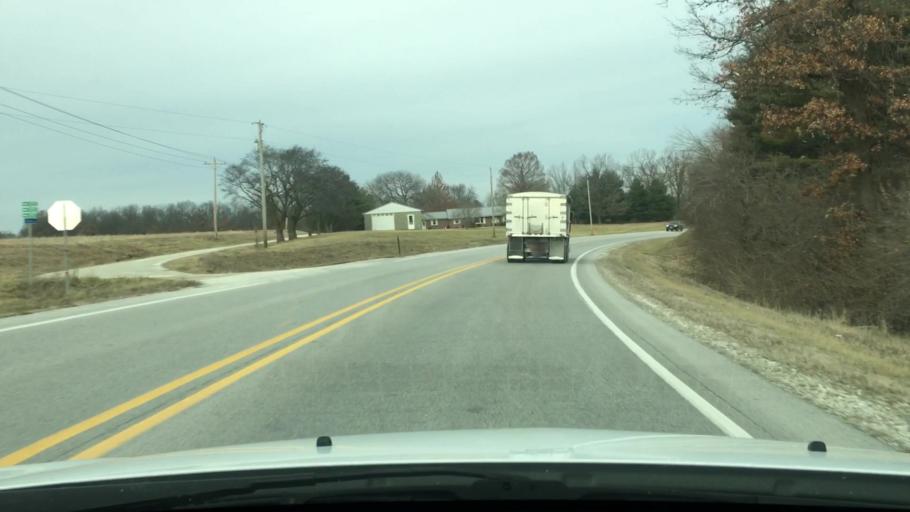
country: US
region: Illinois
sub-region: Pike County
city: Pittsfield
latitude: 39.6523
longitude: -90.7841
